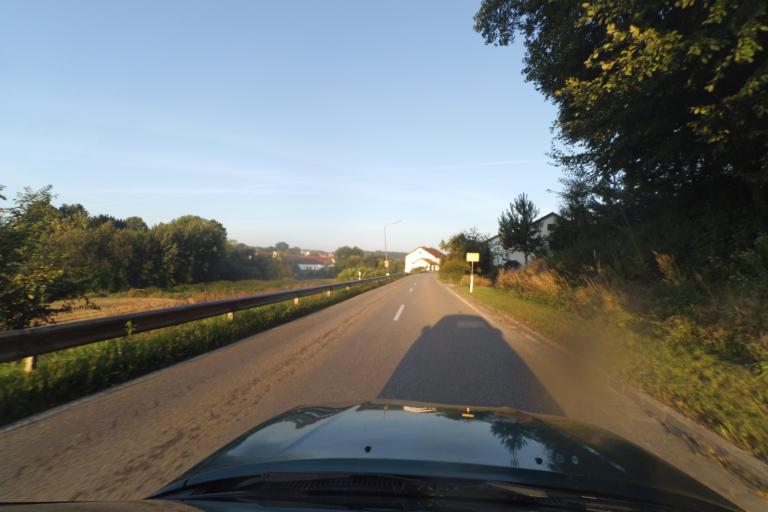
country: DE
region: Bavaria
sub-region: Lower Bavaria
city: Aiglsbach
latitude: 48.6710
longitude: 11.7039
